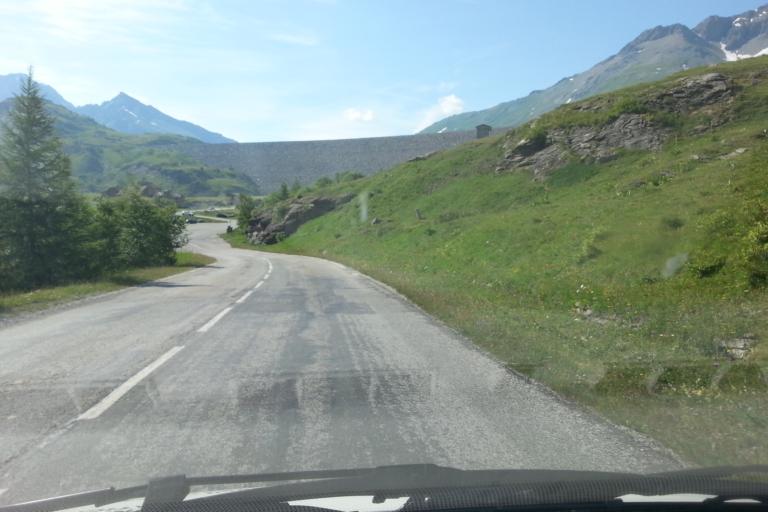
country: IT
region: Piedmont
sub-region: Provincia di Torino
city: Moncenisio
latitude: 45.2181
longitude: 6.9588
